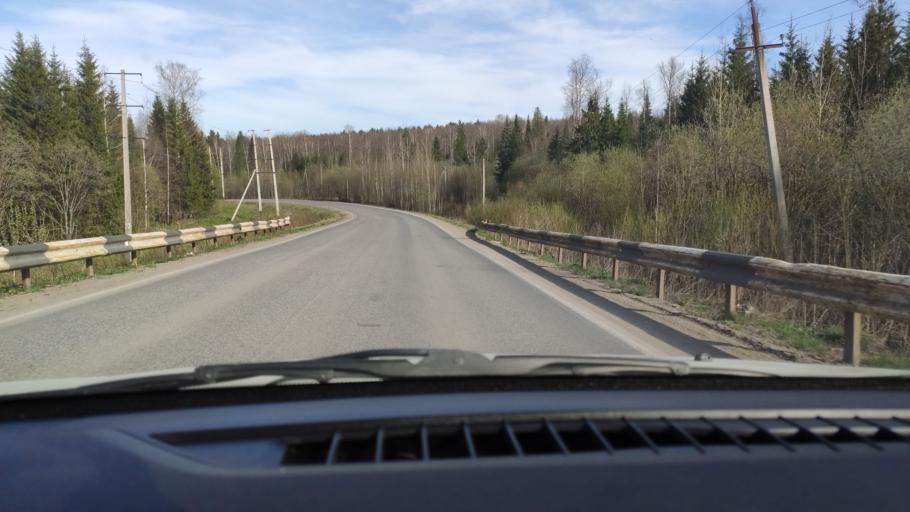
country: RU
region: Perm
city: Novyye Lyady
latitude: 57.9544
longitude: 56.5181
